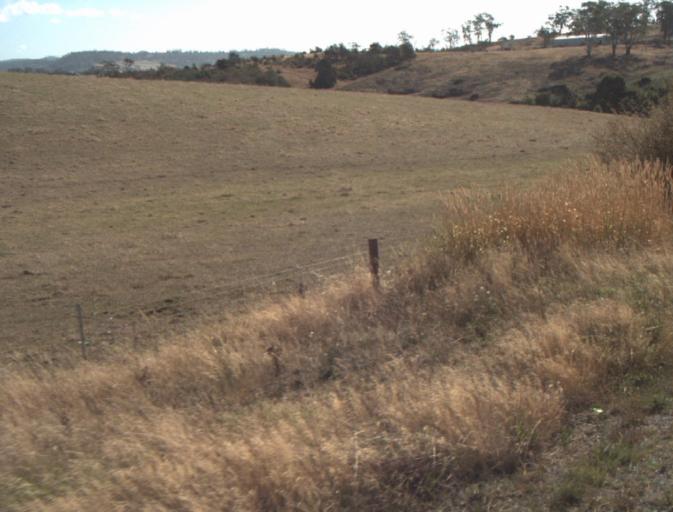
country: AU
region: Tasmania
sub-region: Launceston
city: Mayfield
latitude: -41.3501
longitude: 147.0976
